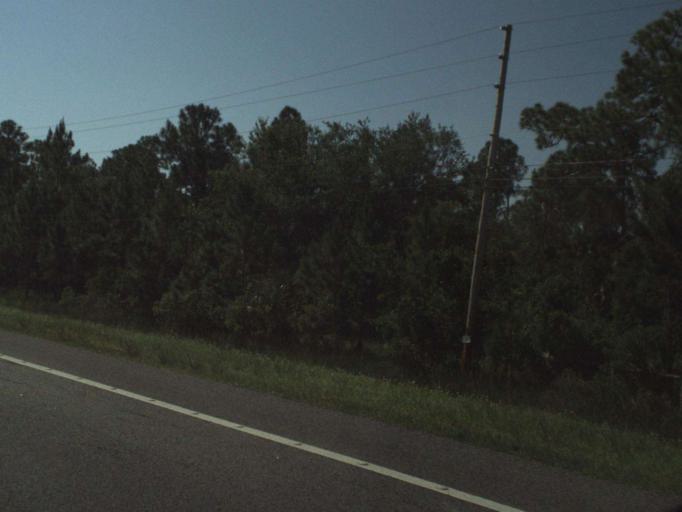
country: US
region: Florida
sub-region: Brevard County
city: Cocoa West
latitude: 28.3813
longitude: -80.9198
